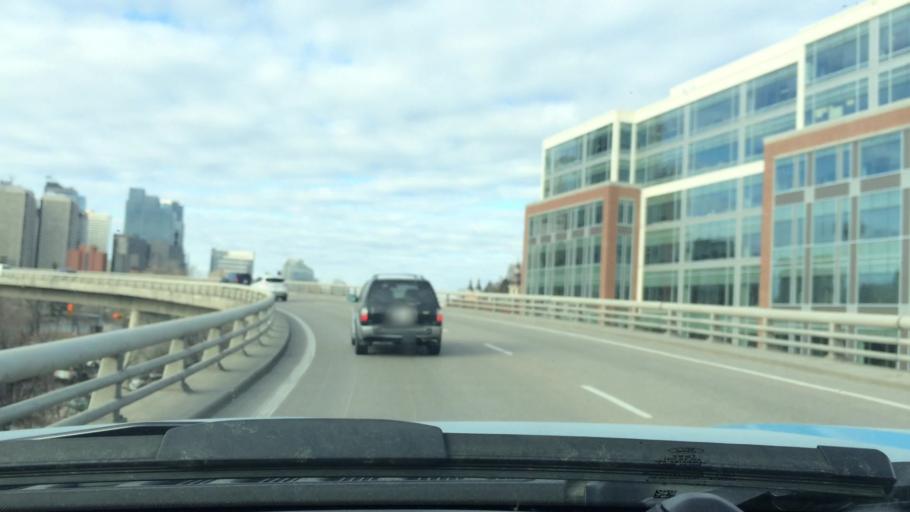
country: CA
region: Alberta
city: Calgary
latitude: 51.0508
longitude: -114.0495
